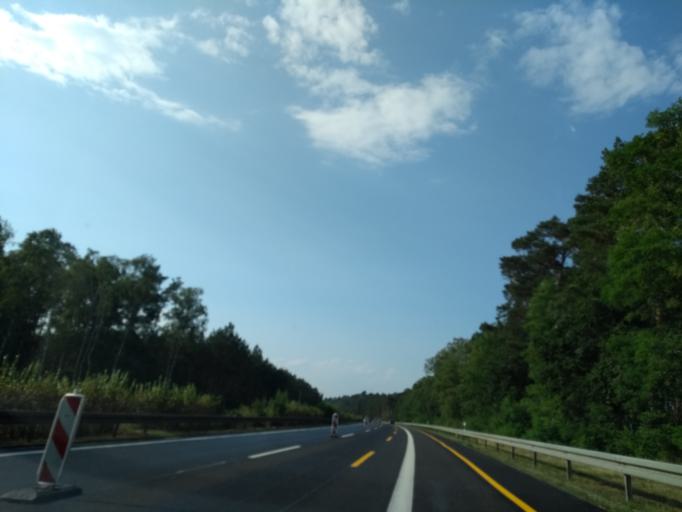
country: DE
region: Brandenburg
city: Bronkow
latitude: 51.6466
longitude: 13.9420
